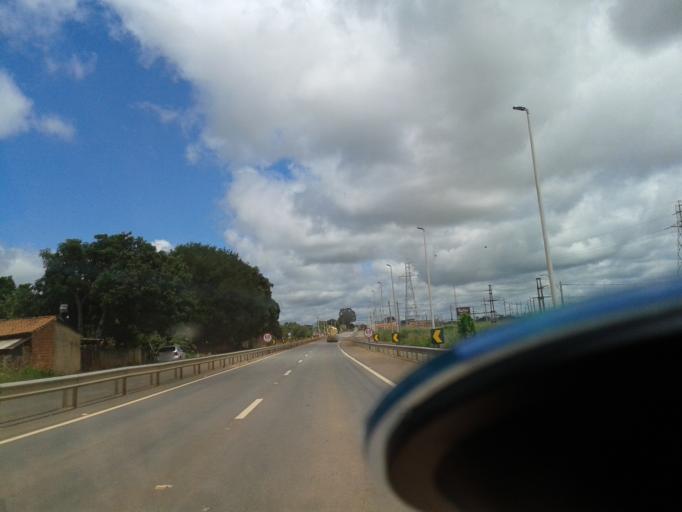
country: BR
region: Goias
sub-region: Itaberai
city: Itaberai
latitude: -16.0528
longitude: -49.7853
